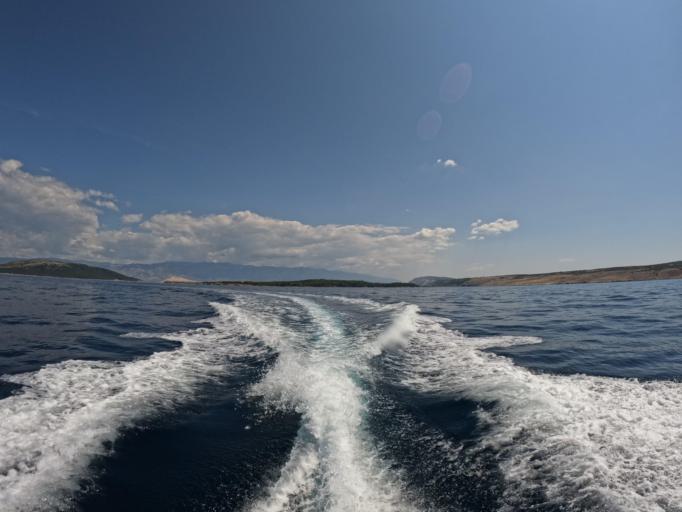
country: HR
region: Primorsko-Goranska
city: Lopar
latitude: 44.8554
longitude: 14.7024
